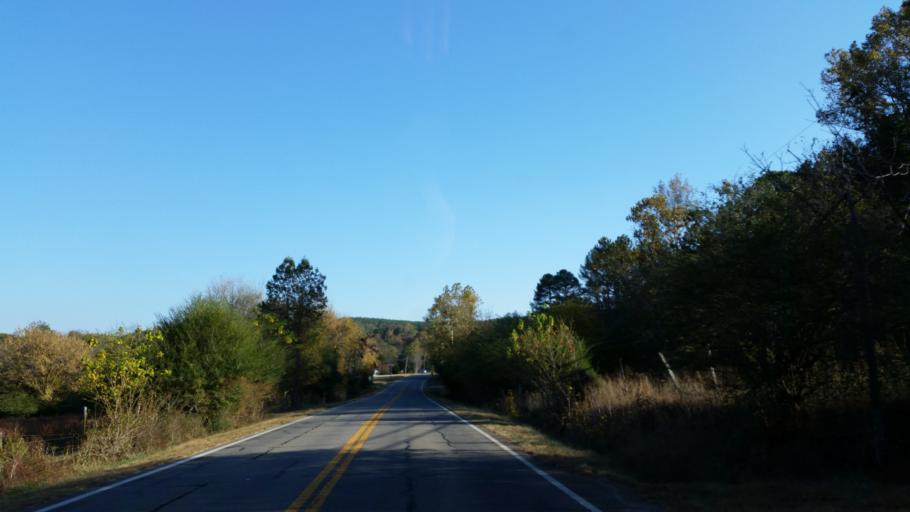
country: US
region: Georgia
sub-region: Pickens County
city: Jasper
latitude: 34.5122
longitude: -84.5156
